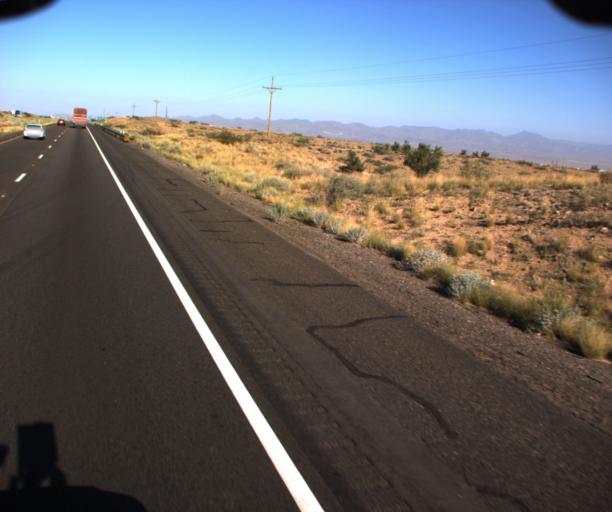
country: US
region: Arizona
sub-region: Mohave County
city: New Kingman-Butler
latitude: 35.1966
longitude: -113.8798
